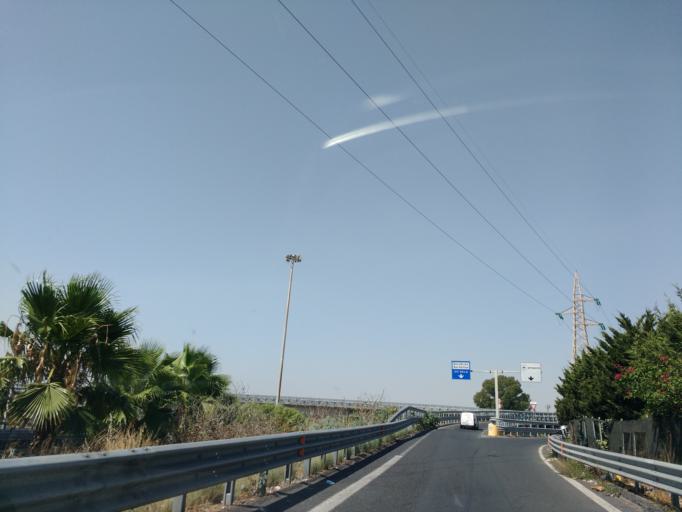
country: IT
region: Sicily
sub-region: Catania
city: Catania
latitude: 37.4791
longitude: 15.0630
